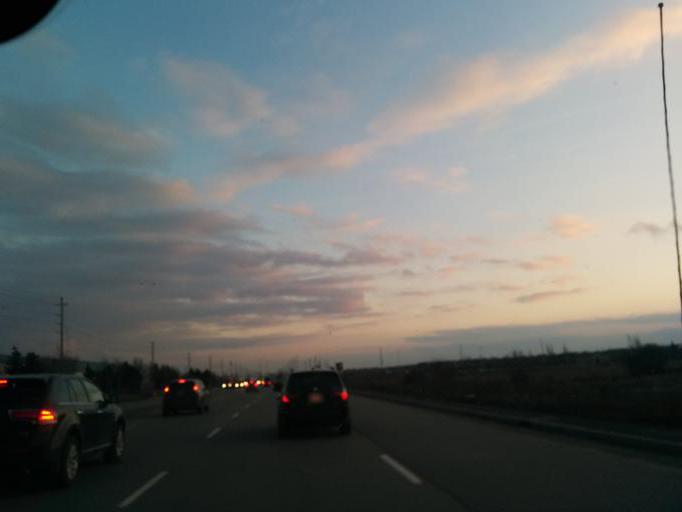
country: CA
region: Ontario
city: Brampton
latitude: 43.8063
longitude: -79.6711
